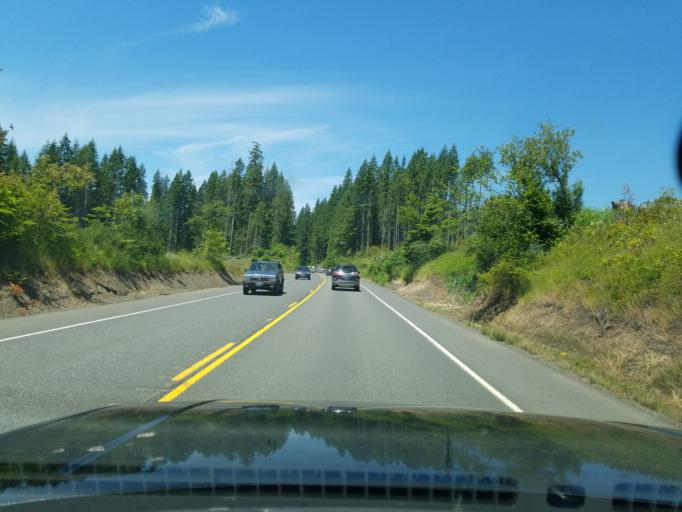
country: US
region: Oregon
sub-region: Columbia County
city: Vernonia
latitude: 45.7709
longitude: -123.3212
